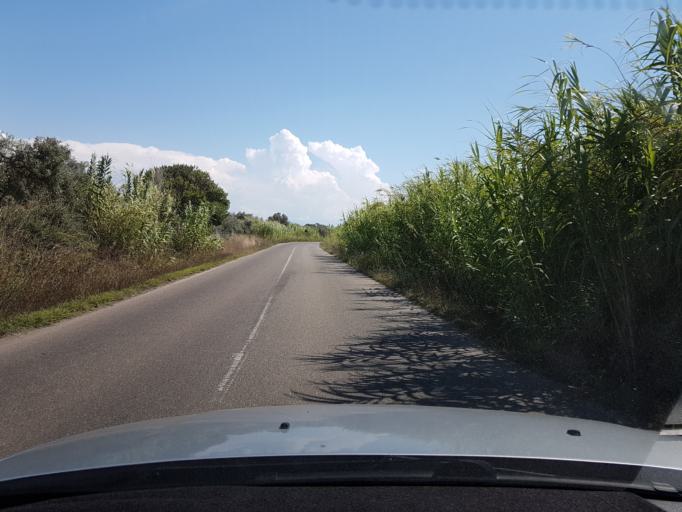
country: IT
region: Sardinia
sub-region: Provincia di Oristano
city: Cabras
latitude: 39.9505
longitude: 8.5302
